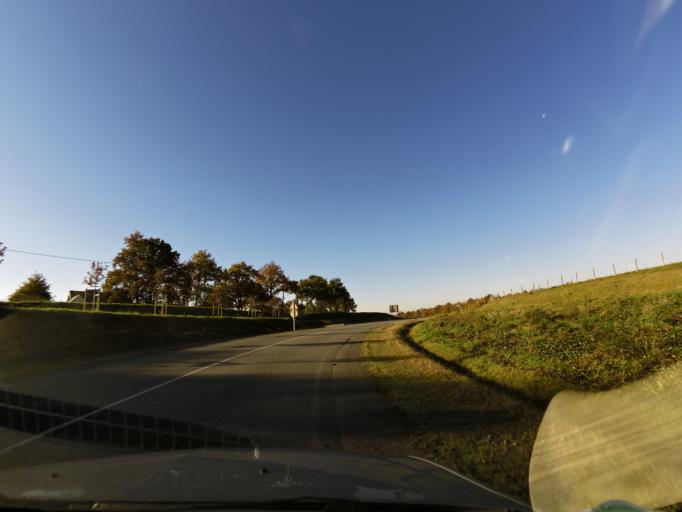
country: FR
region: Brittany
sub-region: Departement d'Ille-et-Vilaine
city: Crevin
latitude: 47.9298
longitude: -1.6701
